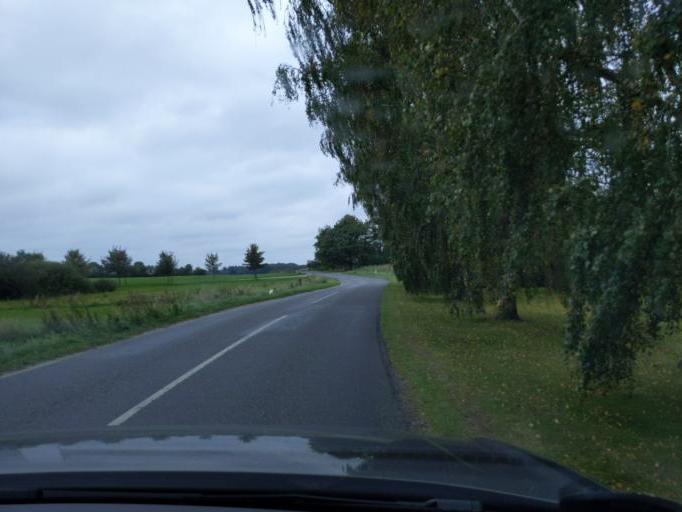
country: DK
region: North Denmark
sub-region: Mariagerfjord Kommune
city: Hobro
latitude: 56.5521
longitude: 9.6562
